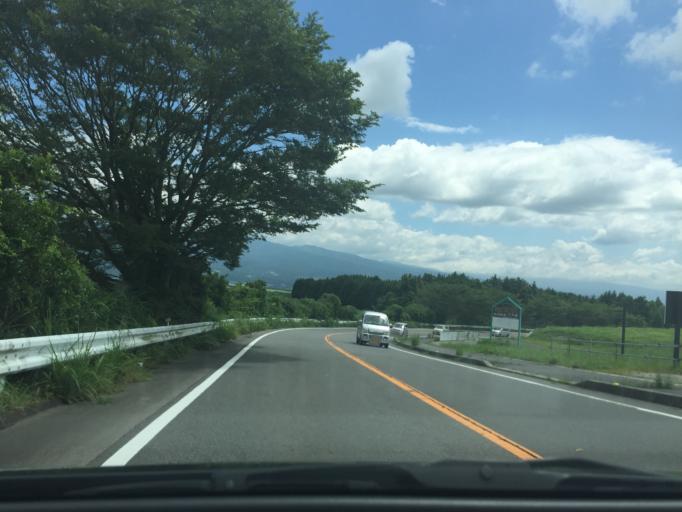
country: JP
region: Shizuoka
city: Gotemba
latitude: 35.2607
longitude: 138.8637
